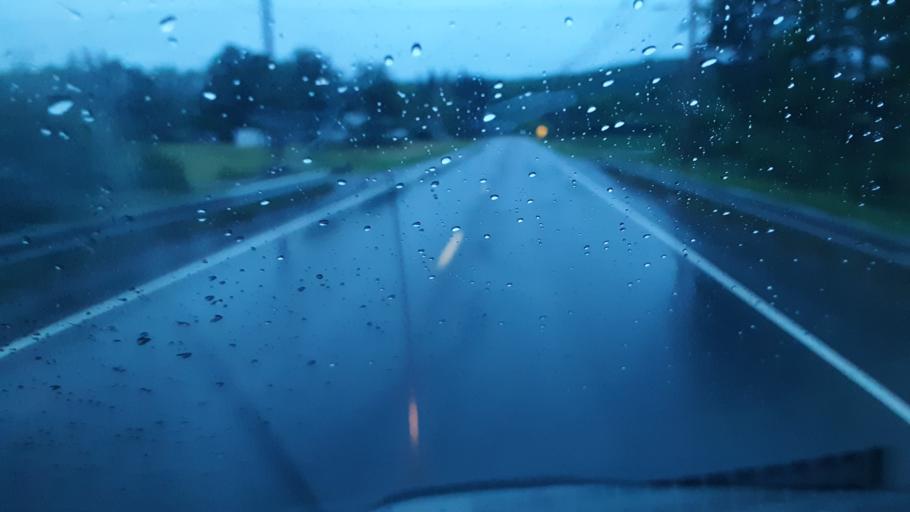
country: US
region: Maine
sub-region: Penobscot County
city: Patten
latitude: 45.8919
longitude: -68.4240
